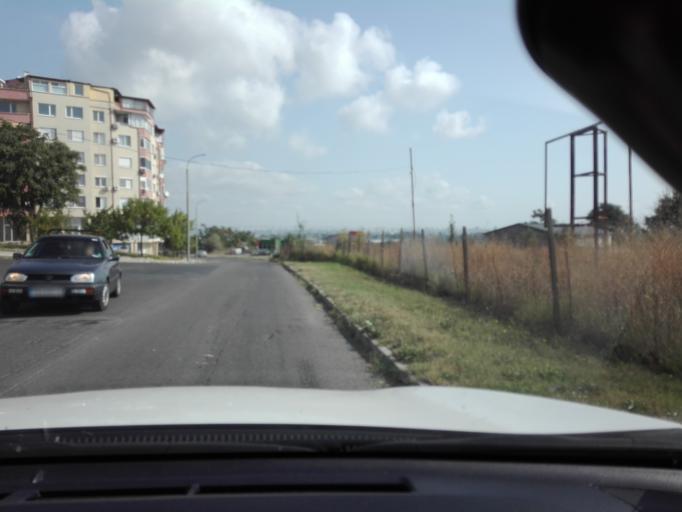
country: BG
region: Burgas
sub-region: Obshtina Burgas
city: Burgas
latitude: 42.4563
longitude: 27.4239
